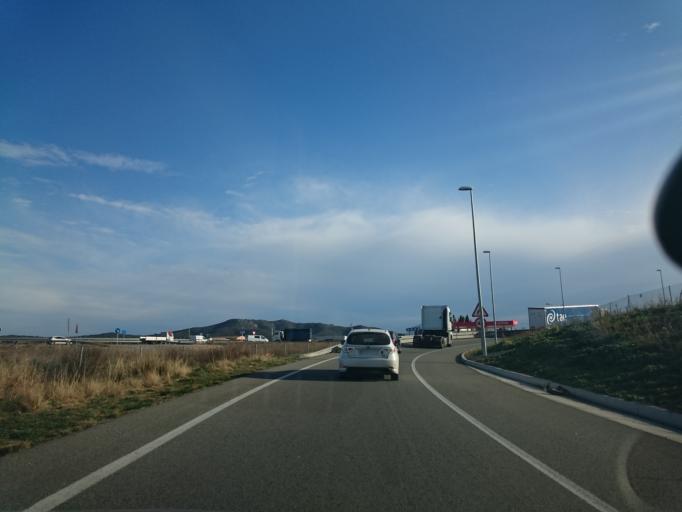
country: ES
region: Catalonia
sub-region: Provincia de Barcelona
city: Vilafranca del Penedes
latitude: 41.3514
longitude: 1.7208
